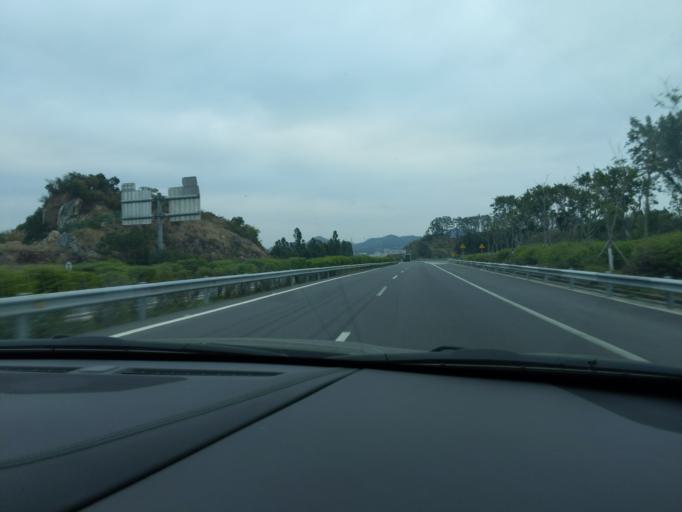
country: CN
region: Fujian
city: Neikeng
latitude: 24.7862
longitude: 118.4796
